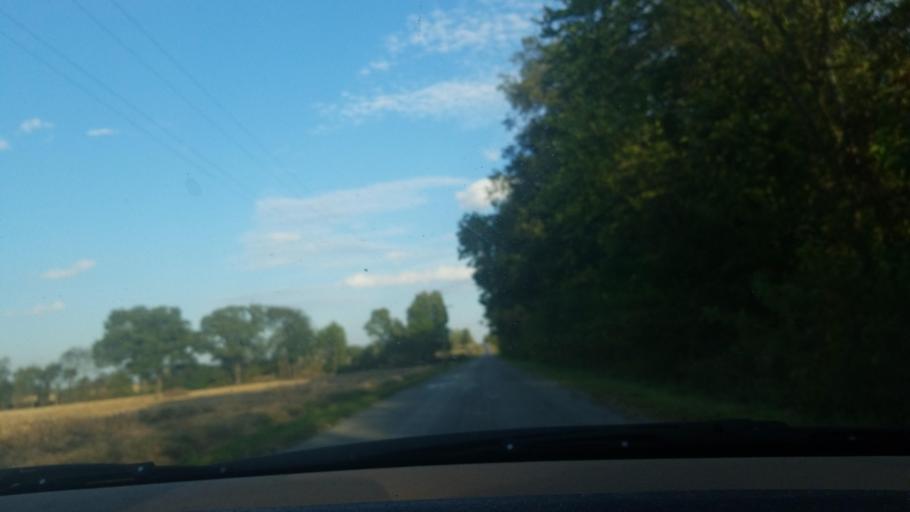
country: US
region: Illinois
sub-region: Saline County
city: Carrier Mills
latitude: 37.8050
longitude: -88.6724
